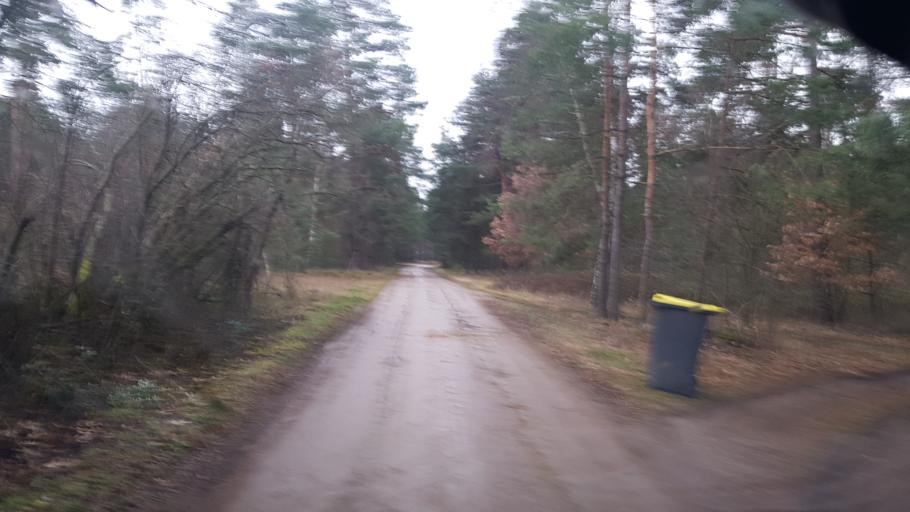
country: DE
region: Brandenburg
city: Sallgast
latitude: 51.6644
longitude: 13.8258
